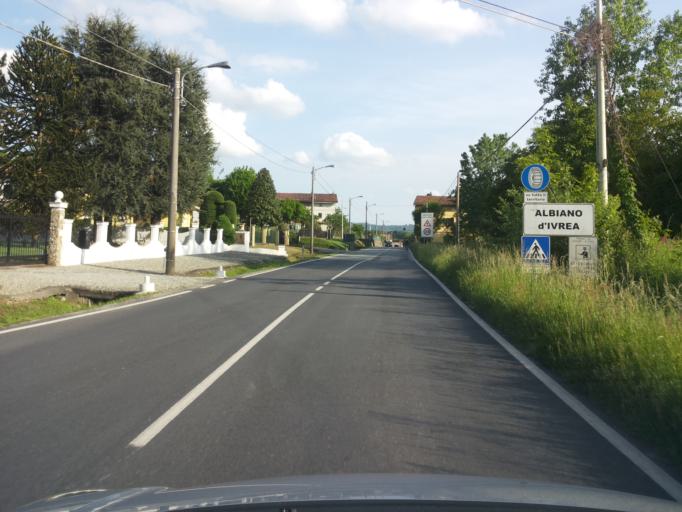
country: IT
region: Piedmont
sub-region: Provincia di Torino
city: Albiano d'Ivrea
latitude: 45.4398
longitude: 7.9440
